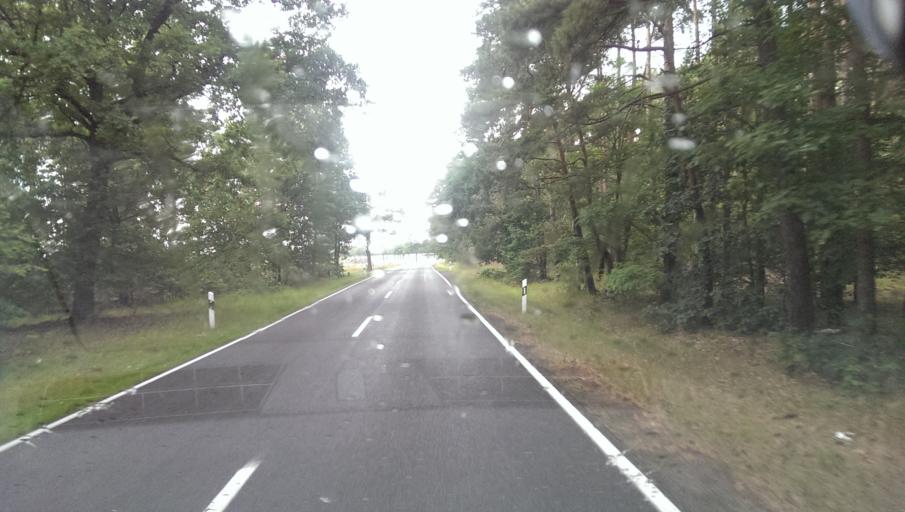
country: DE
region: Brandenburg
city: Borkwalde
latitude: 52.3005
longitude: 12.8009
